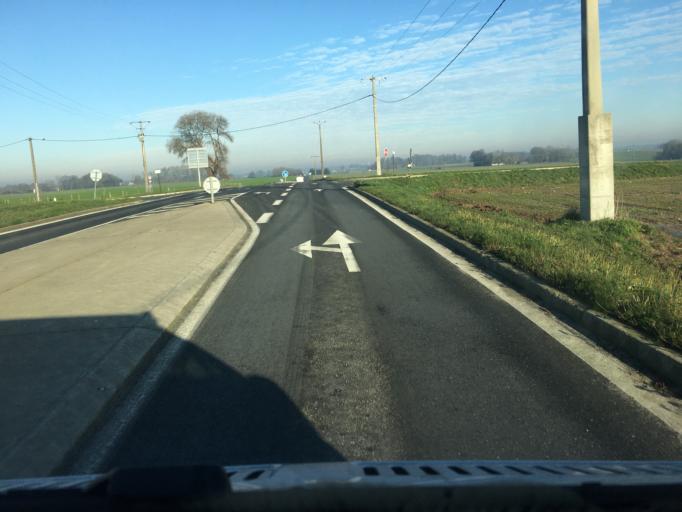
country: FR
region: Haute-Normandie
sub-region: Departement de la Seine-Maritime
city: Auzebosc
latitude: 49.5734
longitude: 0.7271
